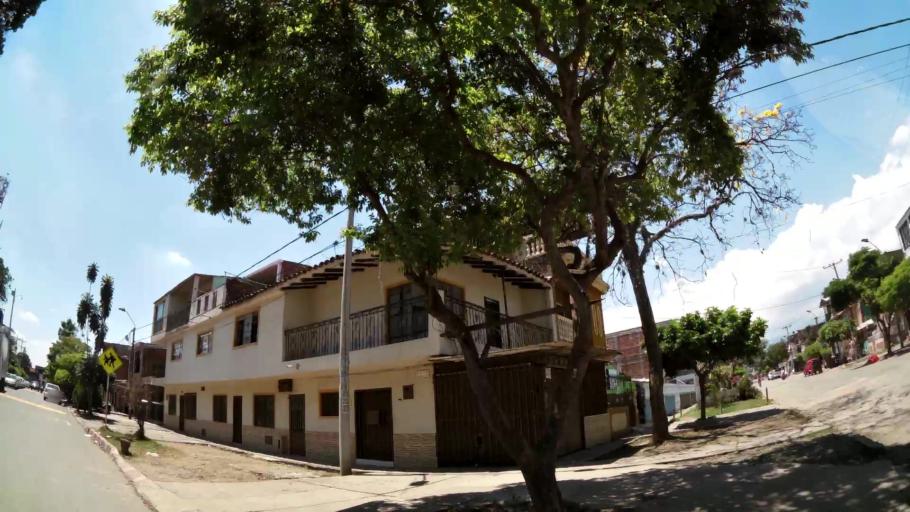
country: CO
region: Valle del Cauca
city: Cali
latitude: 3.4355
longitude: -76.5040
